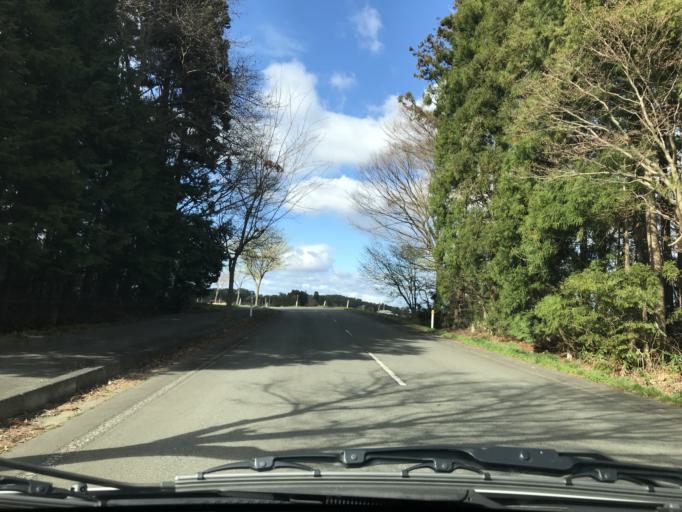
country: JP
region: Iwate
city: Mizusawa
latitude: 39.1095
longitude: 141.0985
